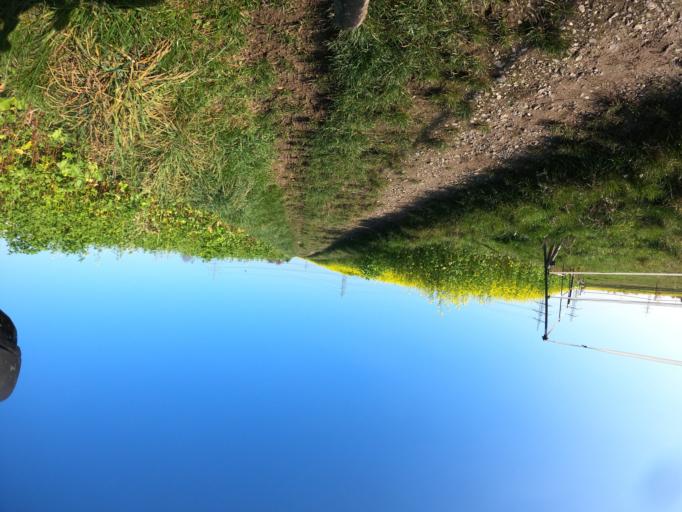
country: DE
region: Baden-Wuerttemberg
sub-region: Regierungsbezirk Stuttgart
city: Magstadt
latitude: 48.7239
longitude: 8.9587
